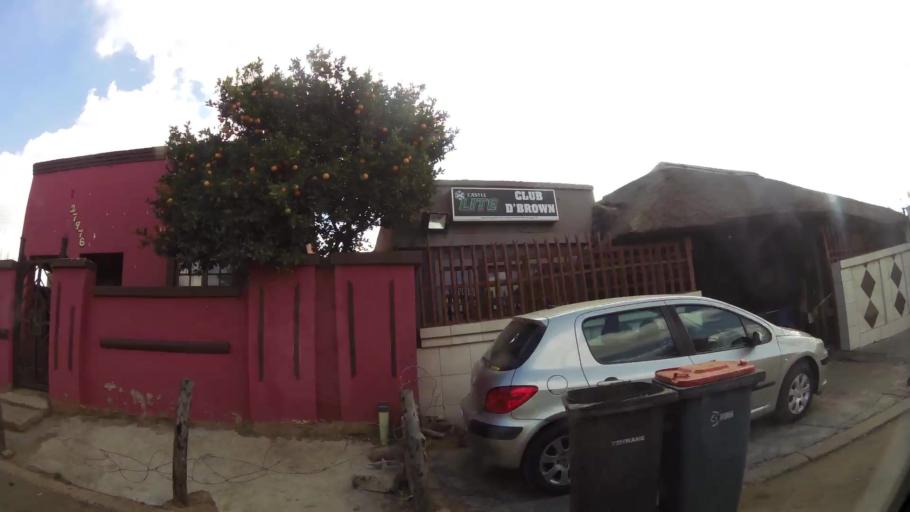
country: ZA
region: Gauteng
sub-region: City of Tshwane Metropolitan Municipality
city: Cullinan
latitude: -25.7016
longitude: 28.3972
